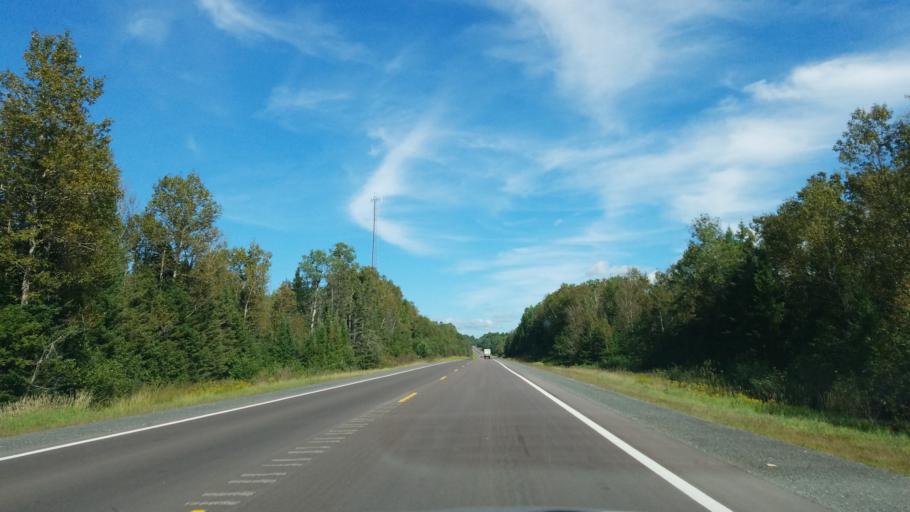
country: US
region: Michigan
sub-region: Baraga County
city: Baraga
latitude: 46.4948
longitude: -88.8200
